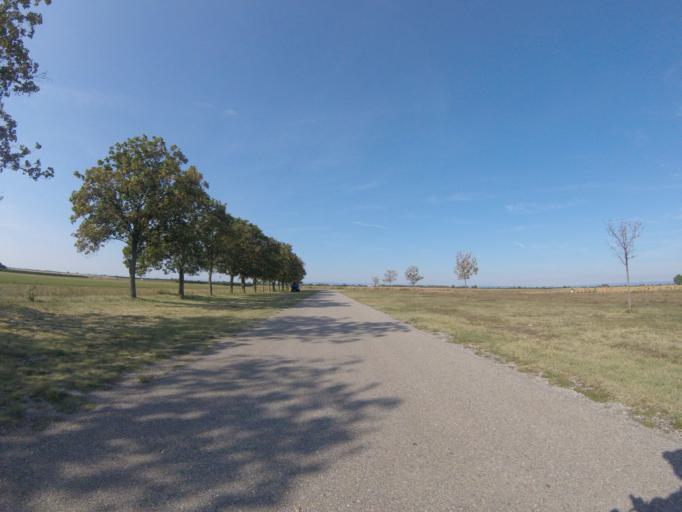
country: AT
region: Burgenland
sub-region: Politischer Bezirk Neusiedl am See
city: Apetlon
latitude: 47.7844
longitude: 16.8345
